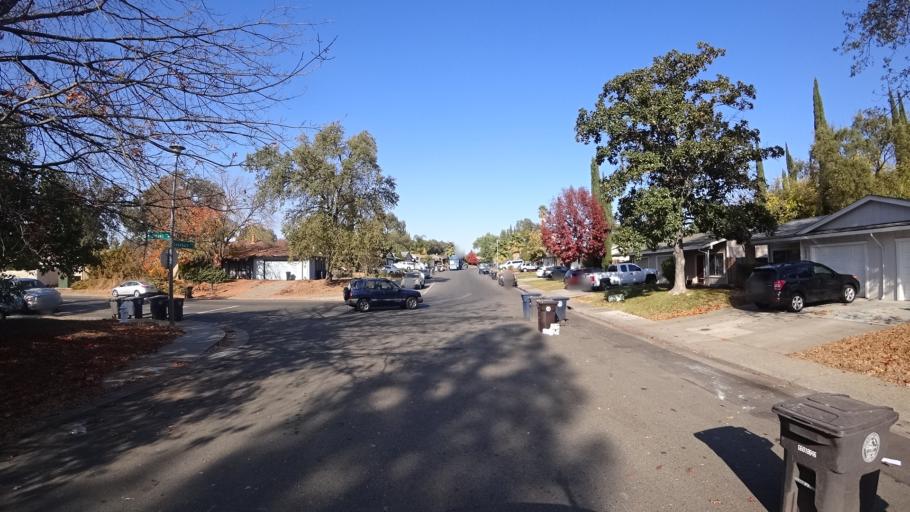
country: US
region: California
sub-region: Sacramento County
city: Citrus Heights
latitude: 38.6822
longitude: -121.2788
